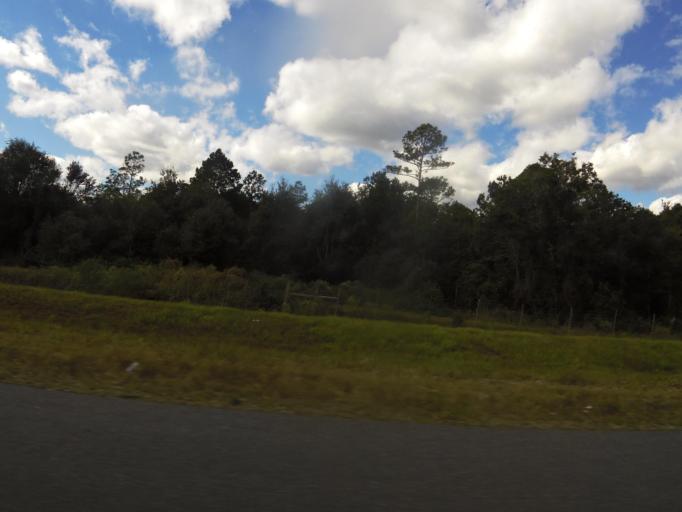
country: US
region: Florida
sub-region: Bradford County
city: Starke
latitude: 29.9552
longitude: -82.1368
